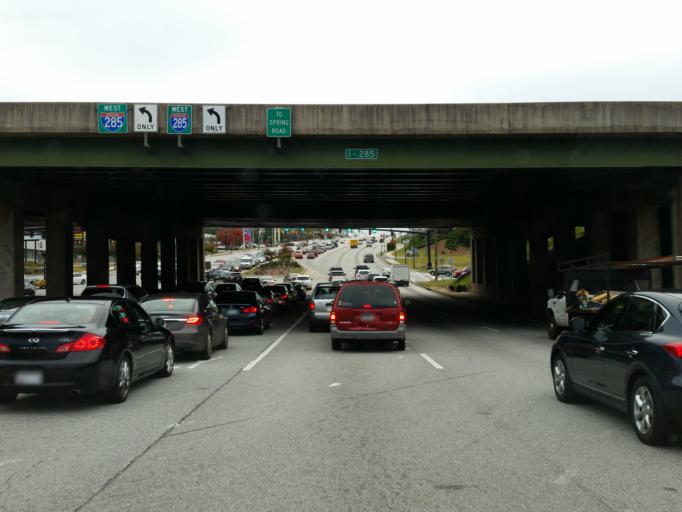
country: US
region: Georgia
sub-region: Cobb County
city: Vinings
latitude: 33.8841
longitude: -84.4695
